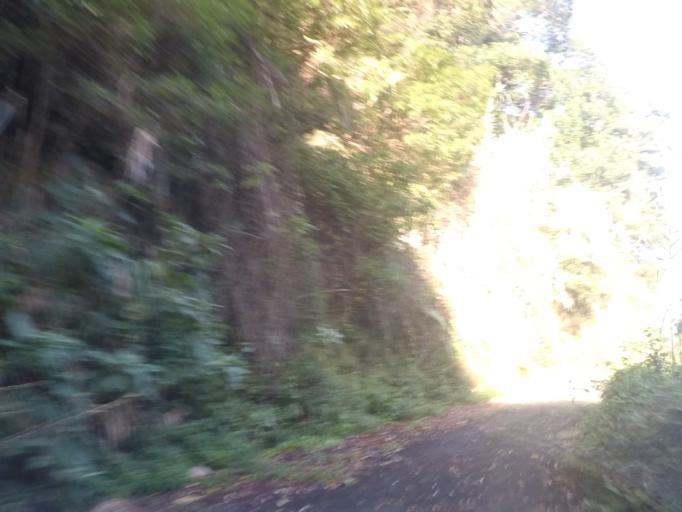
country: PT
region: Madeira
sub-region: Santana
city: Santana
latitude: 32.8165
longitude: -16.8959
